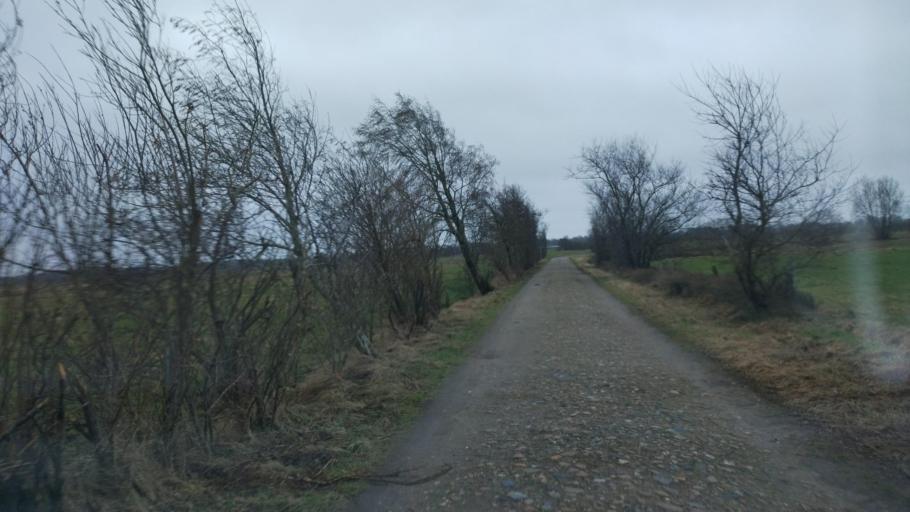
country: DE
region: Schleswig-Holstein
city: Gross Rheide
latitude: 54.4562
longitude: 9.4338
